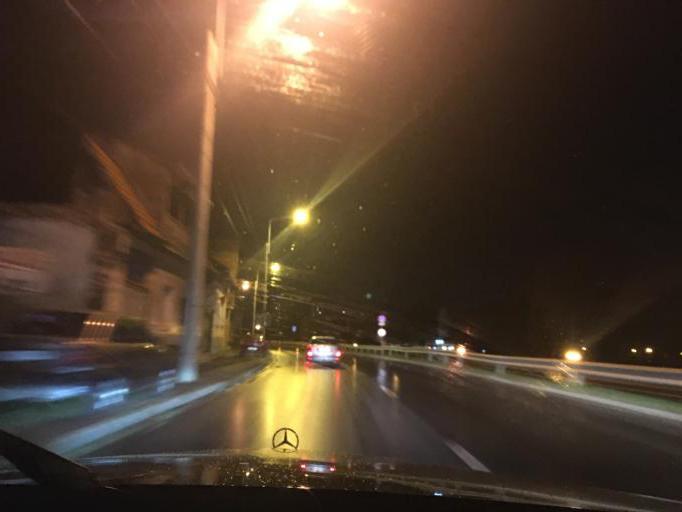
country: RO
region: Bihor
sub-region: Comuna Biharea
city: Oradea
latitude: 47.0534
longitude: 21.9475
